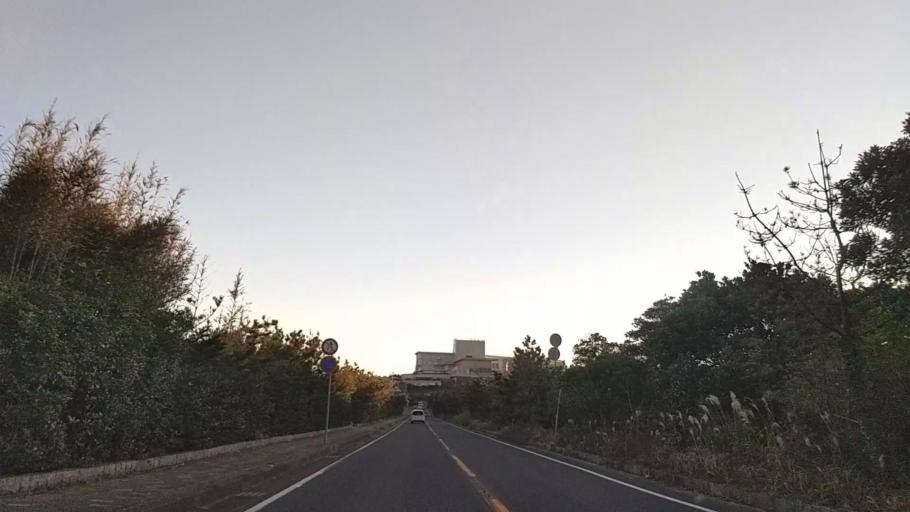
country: JP
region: Chiba
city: Hasaki
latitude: 35.7119
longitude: 140.8650
